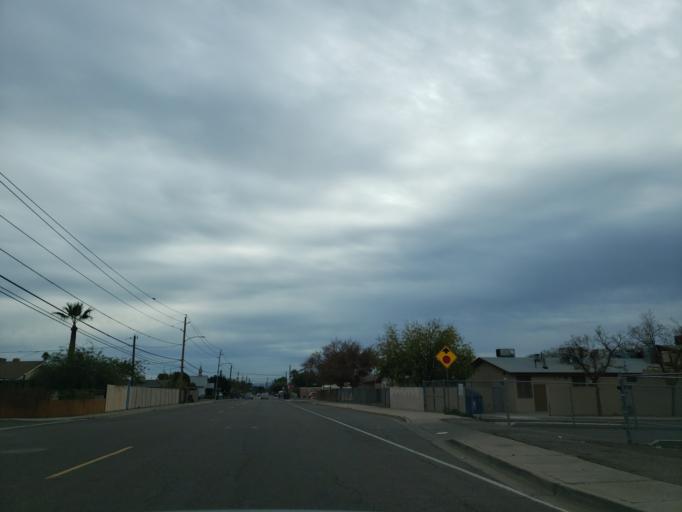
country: US
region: Arizona
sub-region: Maricopa County
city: Glendale
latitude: 33.5760
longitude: -112.0913
